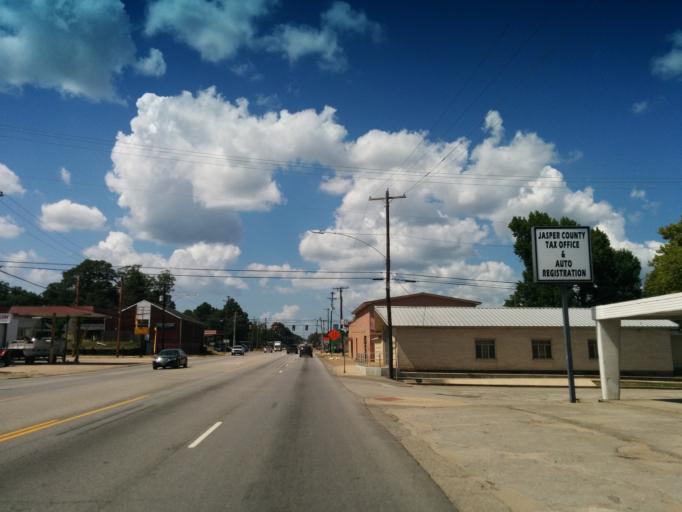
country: US
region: Texas
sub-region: Jasper County
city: Jasper
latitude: 30.9216
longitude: -93.9967
